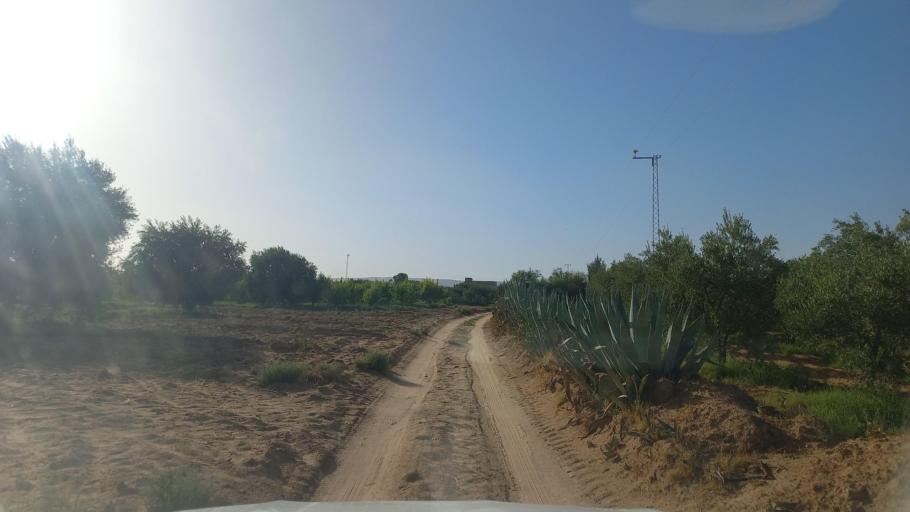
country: TN
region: Al Qasrayn
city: Kasserine
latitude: 35.2629
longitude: 9.0263
